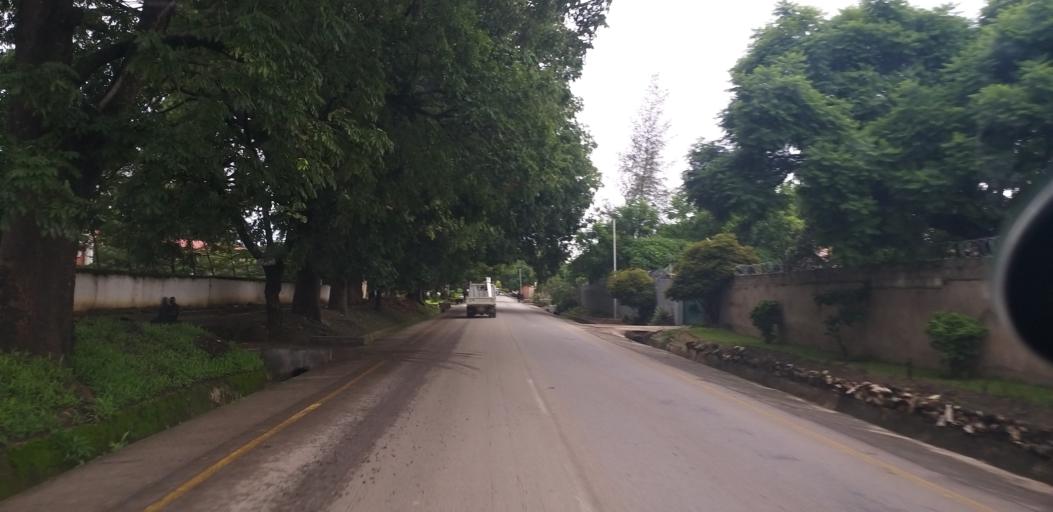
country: ZM
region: Lusaka
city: Lusaka
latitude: -15.4206
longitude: 28.2961
